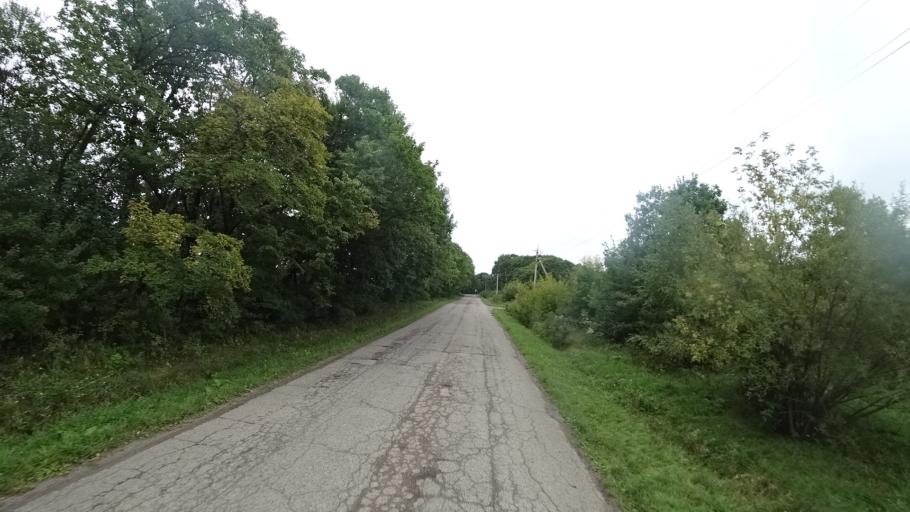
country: RU
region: Primorskiy
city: Chernigovka
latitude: 44.4556
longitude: 132.5944
